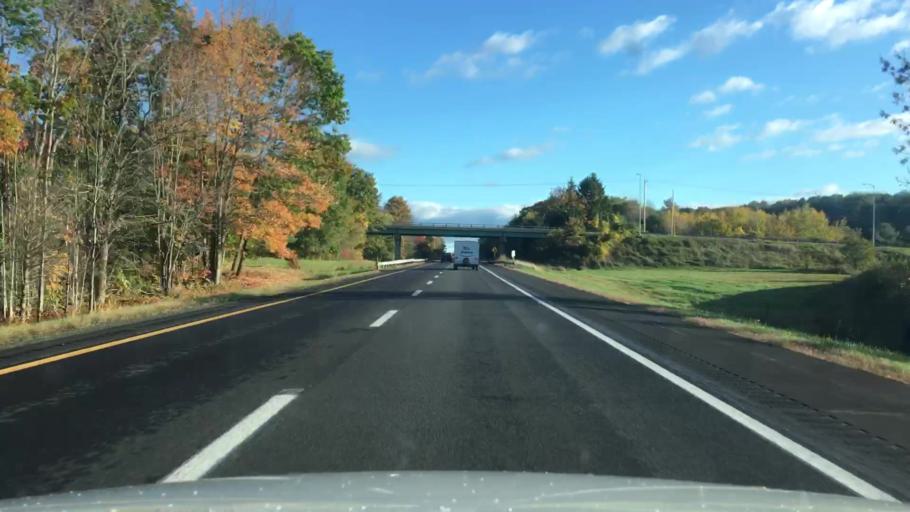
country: US
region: Maine
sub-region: Penobscot County
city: Veazie
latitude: 44.8718
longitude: -68.7032
